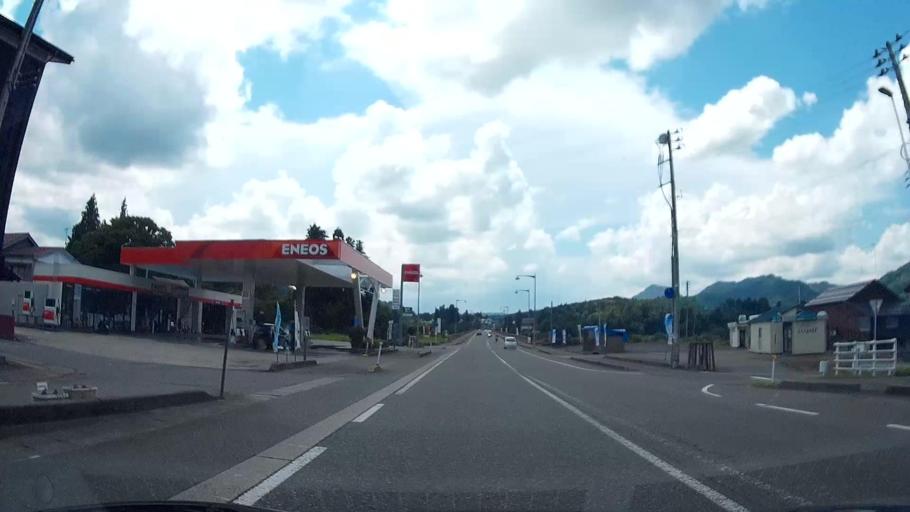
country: JP
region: Niigata
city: Tokamachi
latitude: 37.0469
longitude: 138.6904
